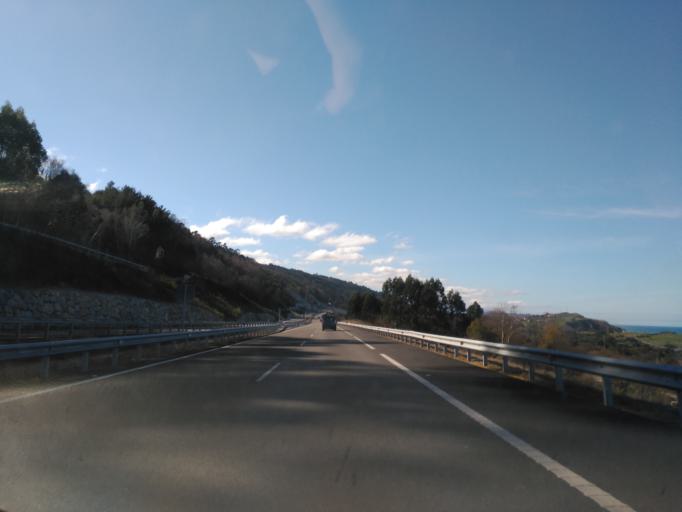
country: ES
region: Cantabria
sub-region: Provincia de Cantabria
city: Tresviso
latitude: 43.3928
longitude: -4.6041
